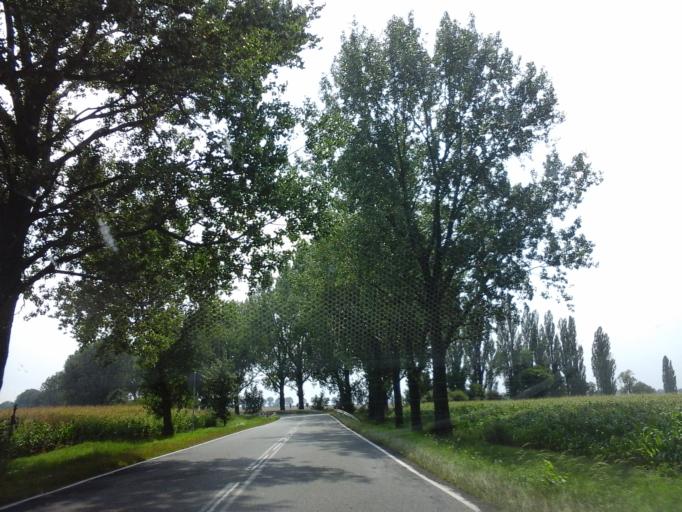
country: PL
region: Lower Silesian Voivodeship
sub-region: Powiat wroclawski
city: Zorawina
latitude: 50.8902
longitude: 17.0615
